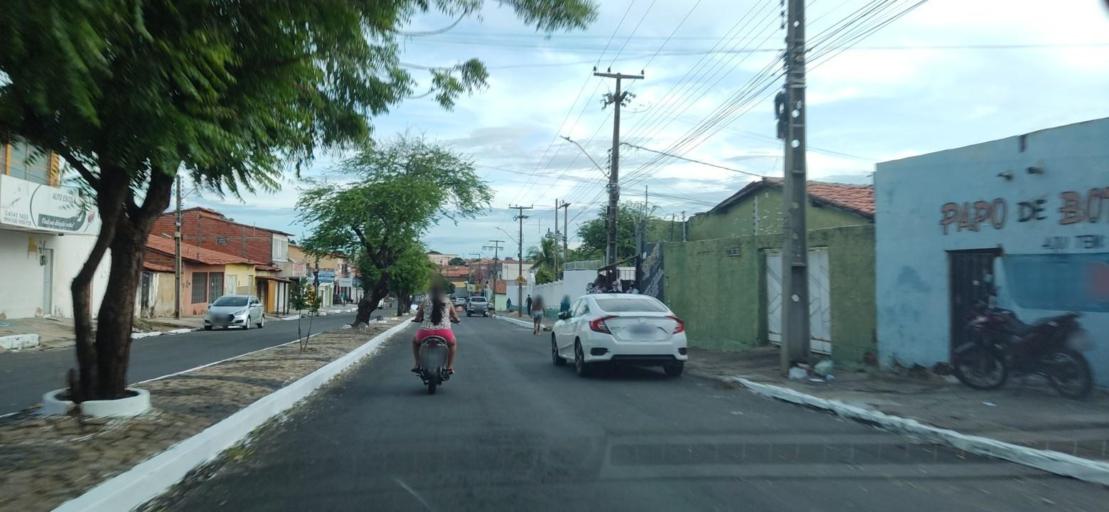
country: BR
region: Piaui
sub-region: Teresina
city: Teresina
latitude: -5.1509
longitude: -42.7876
